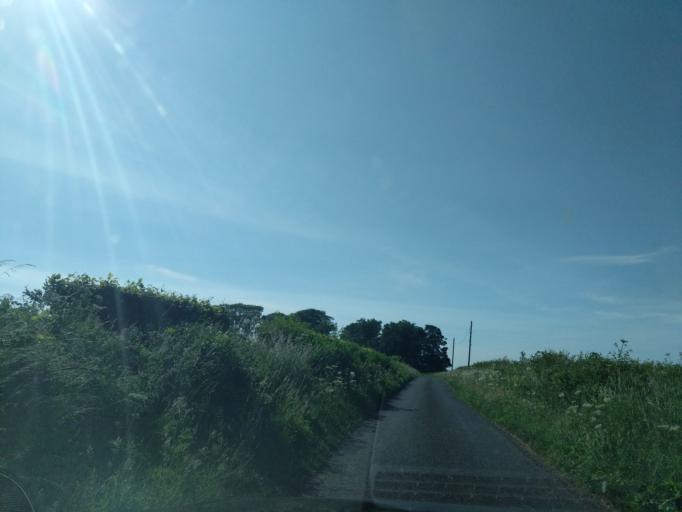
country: GB
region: Scotland
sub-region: East Lothian
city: Ormiston
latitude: 55.8776
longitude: -2.9379
